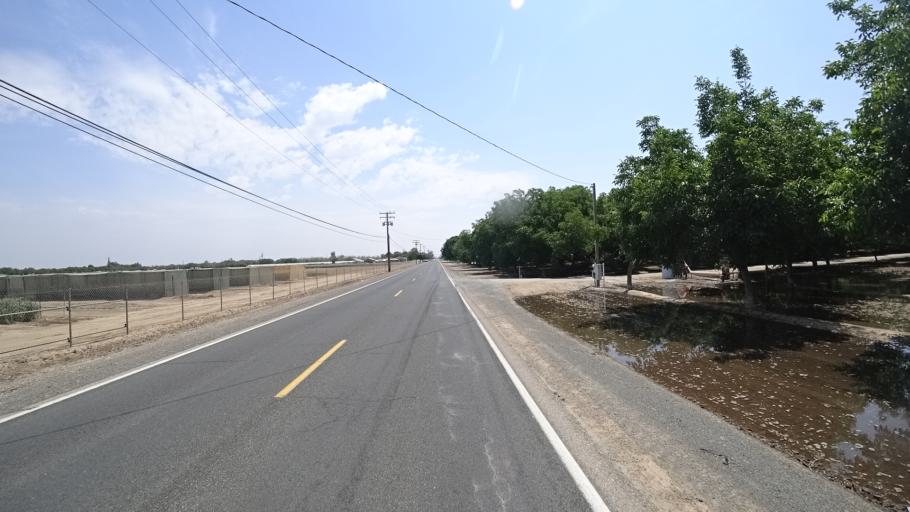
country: US
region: California
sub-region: Kings County
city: Armona
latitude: 36.3280
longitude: -119.7156
